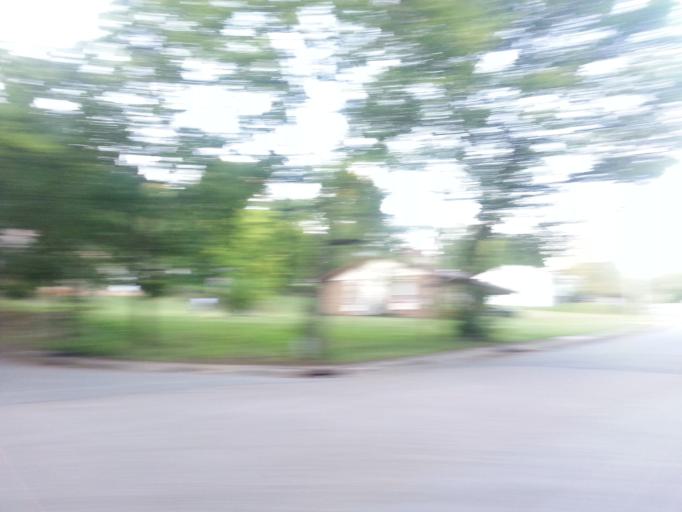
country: US
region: Tennessee
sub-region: Knox County
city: Knoxville
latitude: 35.9691
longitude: -83.8989
